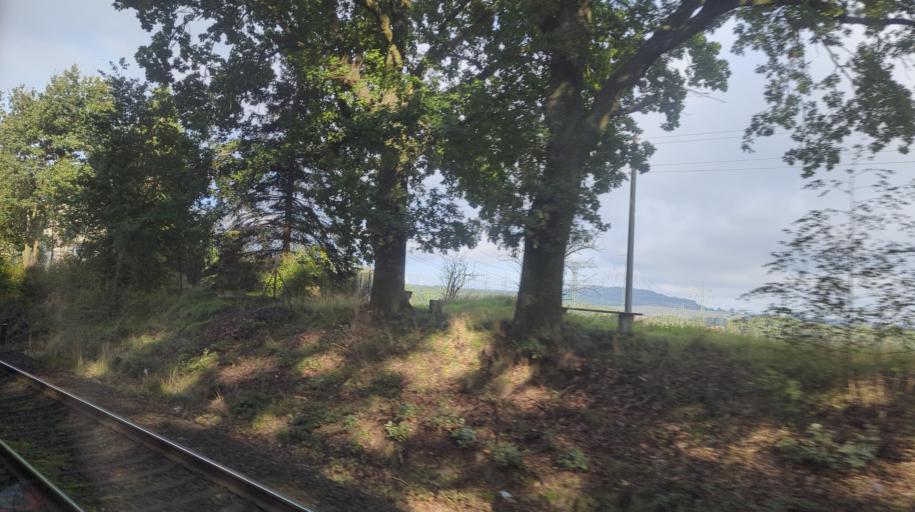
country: DE
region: Saxony
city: Demitz-Thumitz
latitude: 51.1435
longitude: 14.2344
